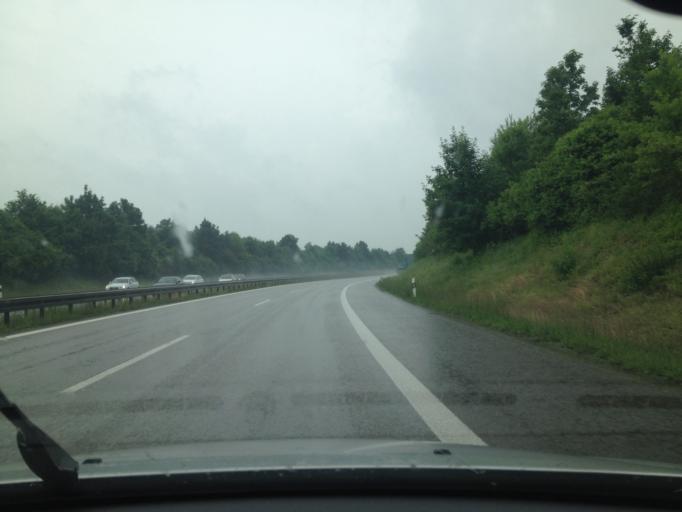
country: DE
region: Bavaria
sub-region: Swabia
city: Klosterlechfeld
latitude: 48.1620
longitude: 10.8371
